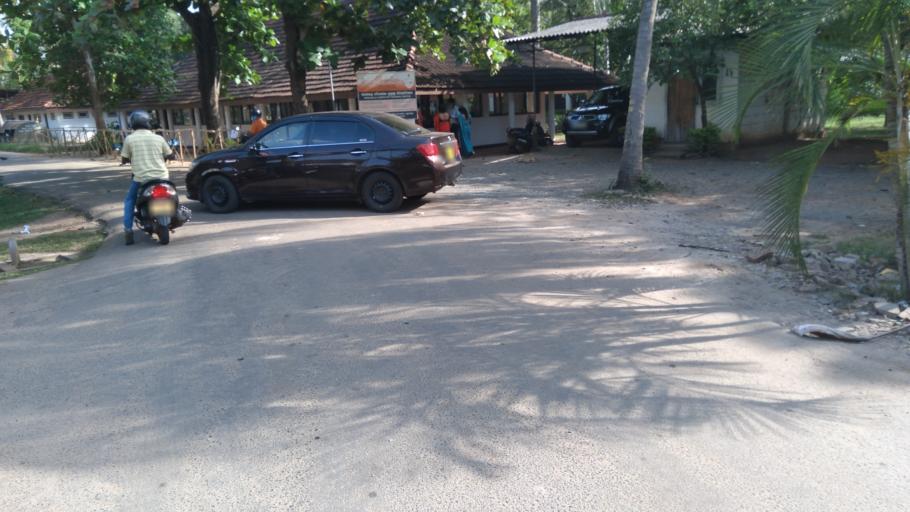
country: LK
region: North Central
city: Anuradhapura
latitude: 8.3274
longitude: 80.4068
